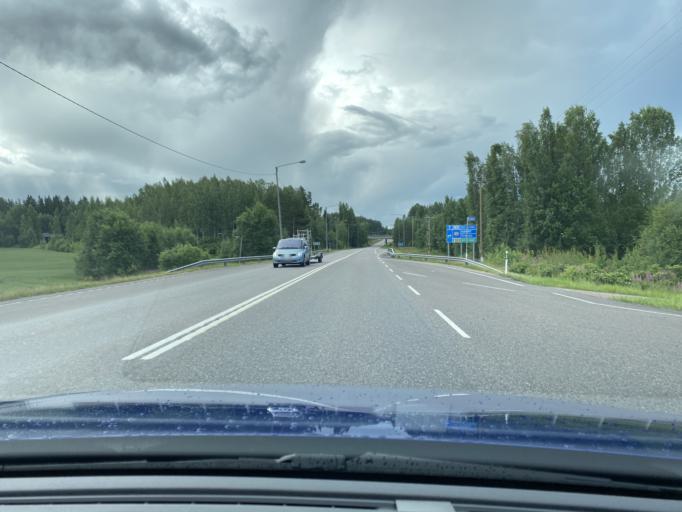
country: FI
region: Uusimaa
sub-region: Helsinki
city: Hyvinge
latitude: 60.5660
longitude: 24.8115
